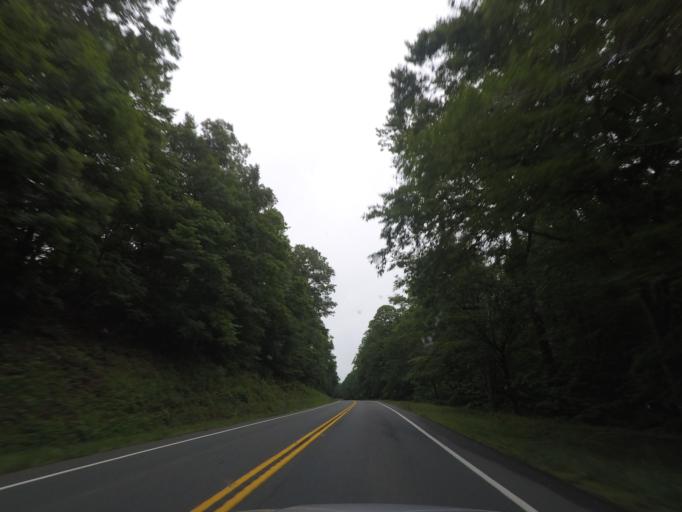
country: US
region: Virginia
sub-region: Fluvanna County
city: Weber City
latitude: 37.7213
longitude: -78.2994
